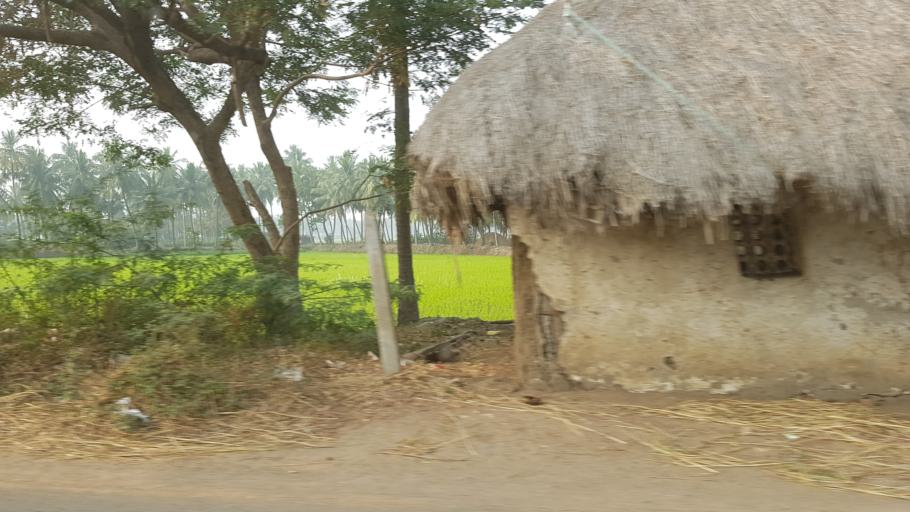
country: IN
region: Andhra Pradesh
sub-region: West Godavari
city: Akividu
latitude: 16.5321
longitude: 81.3920
